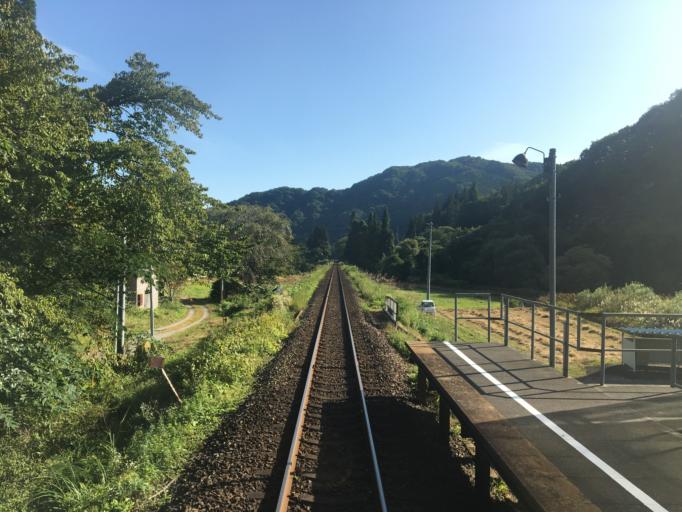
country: JP
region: Akita
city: Kakunodatemachi
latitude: 39.8017
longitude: 140.5860
